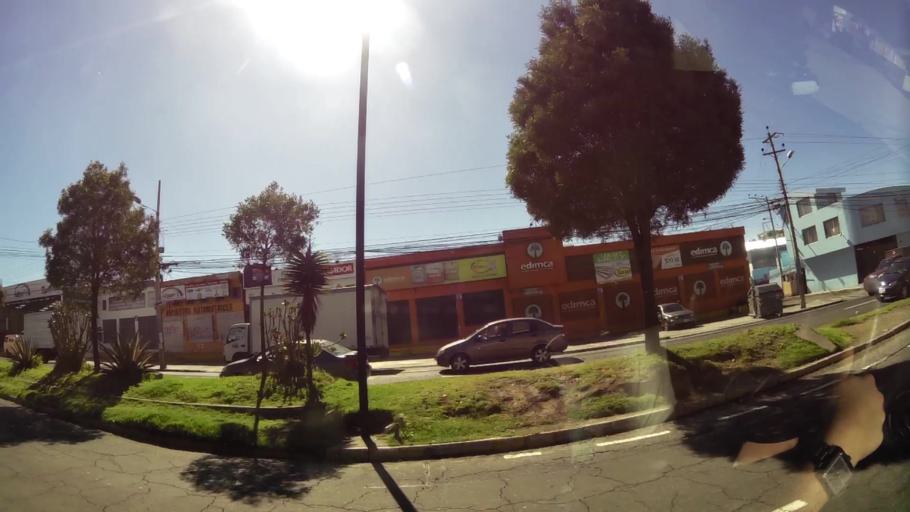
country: EC
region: Pichincha
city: Quito
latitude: -0.1274
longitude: -78.4713
